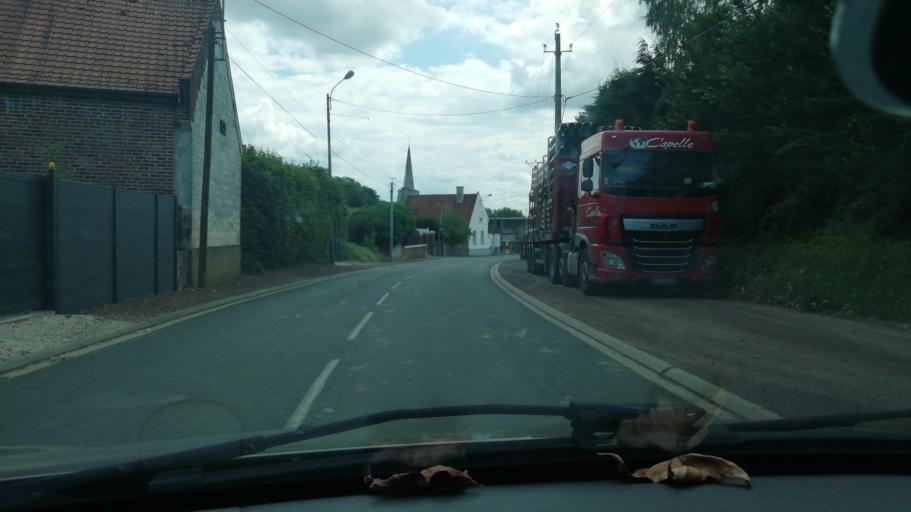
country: FR
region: Nord-Pas-de-Calais
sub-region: Departement du Pas-de-Calais
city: Aubigny-en-Artois
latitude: 50.3264
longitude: 2.5879
